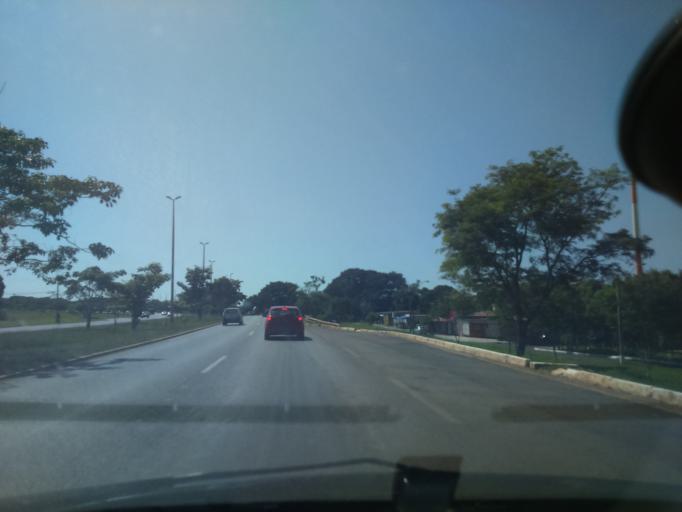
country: BR
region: Federal District
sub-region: Brasilia
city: Brasilia
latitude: -15.8456
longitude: -47.9244
